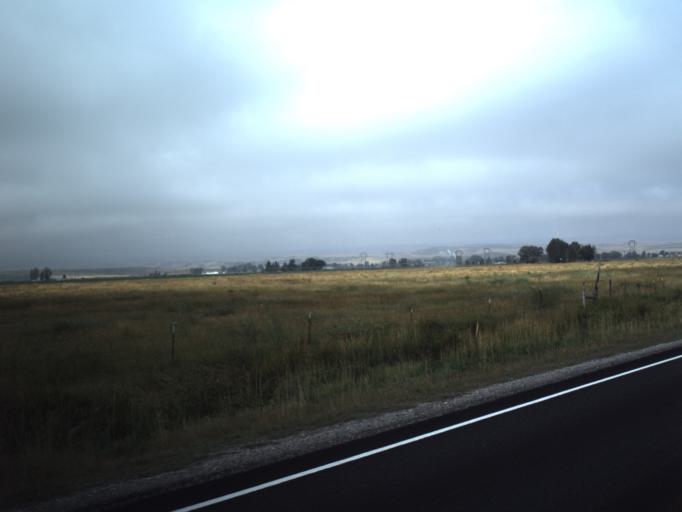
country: US
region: Utah
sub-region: Rich County
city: Randolph
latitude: 41.5156
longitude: -111.1373
